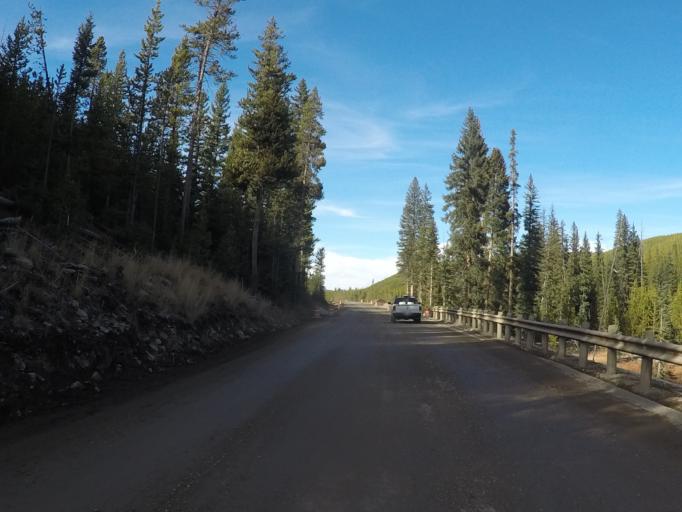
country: US
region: Montana
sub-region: Gallatin County
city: West Yellowstone
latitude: 44.8315
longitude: -110.7283
